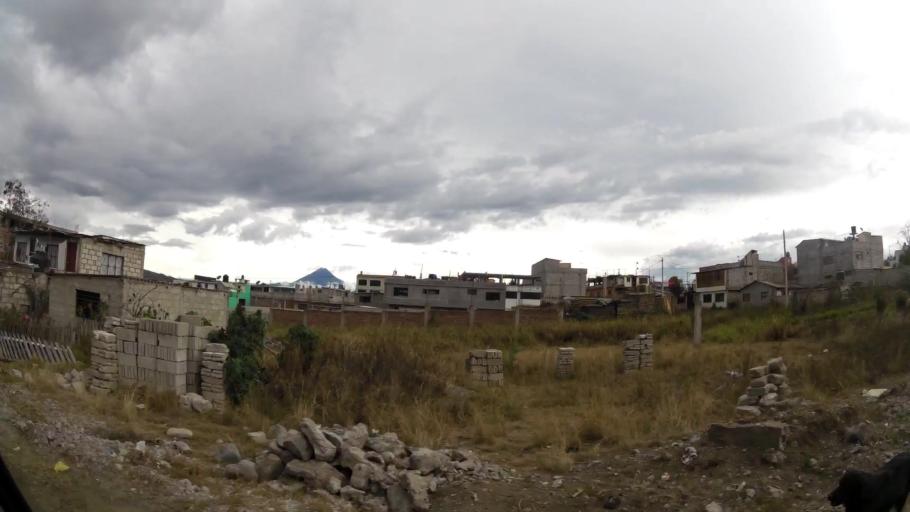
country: EC
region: Tungurahua
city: Ambato
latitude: -1.2692
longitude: -78.6189
